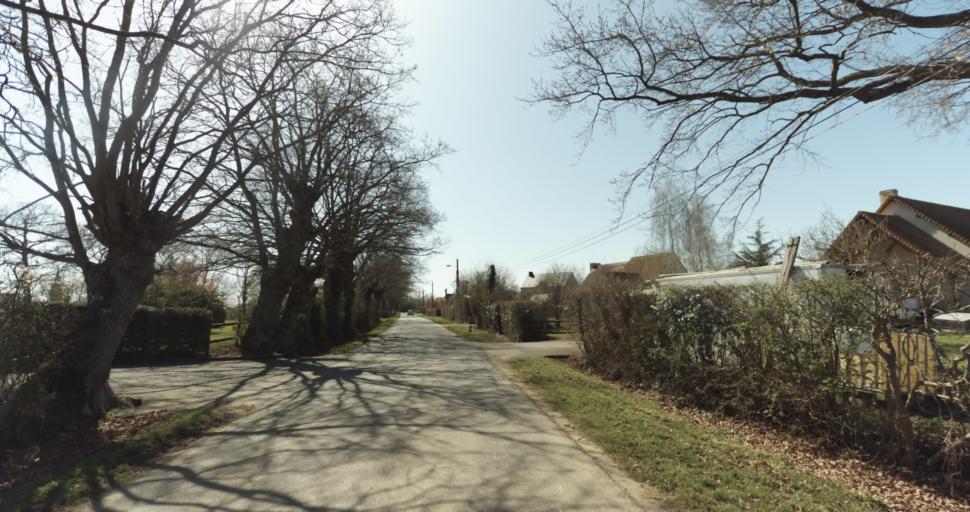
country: FR
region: Lower Normandy
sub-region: Departement du Calvados
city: Saint-Pierre-sur-Dives
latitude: 49.0088
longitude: -0.0073
